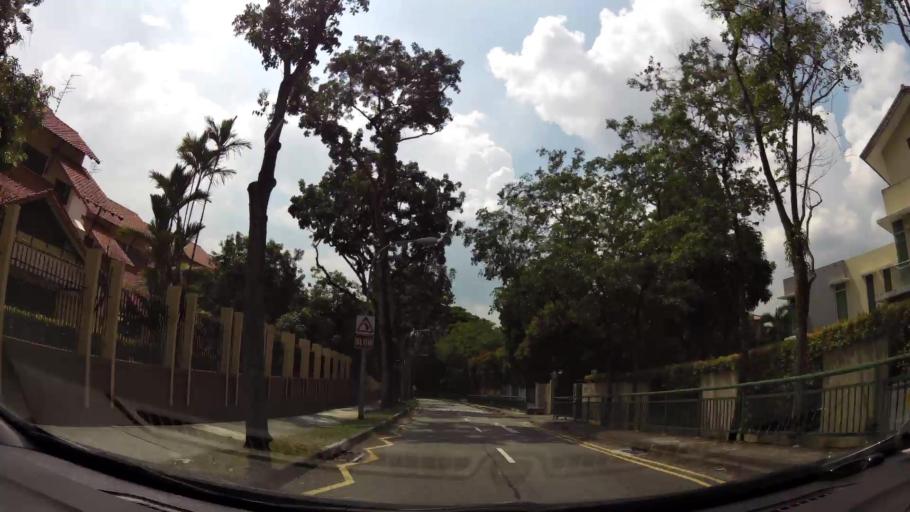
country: SG
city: Singapore
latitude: 1.2957
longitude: 103.8253
